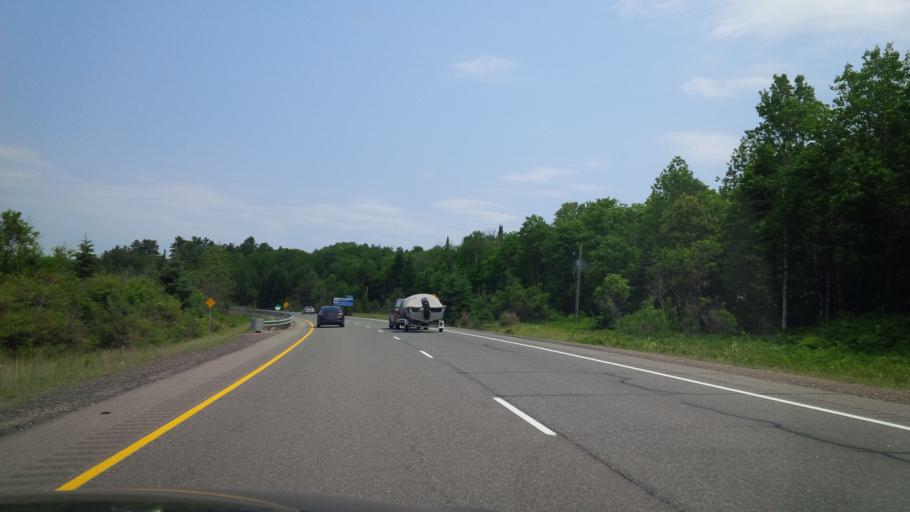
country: CA
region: Ontario
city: Huntsville
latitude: 45.3542
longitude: -79.2224
